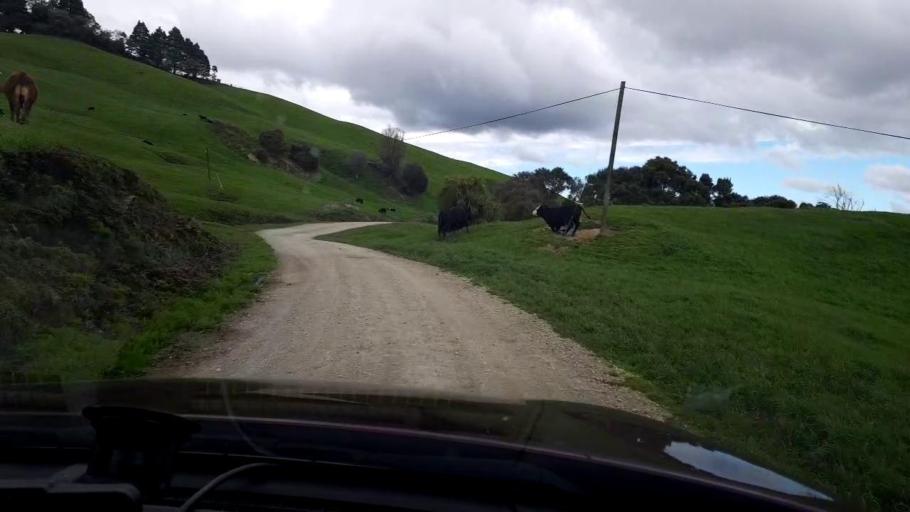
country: NZ
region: Gisborne
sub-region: Gisborne District
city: Gisborne
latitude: -38.3685
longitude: 177.9667
